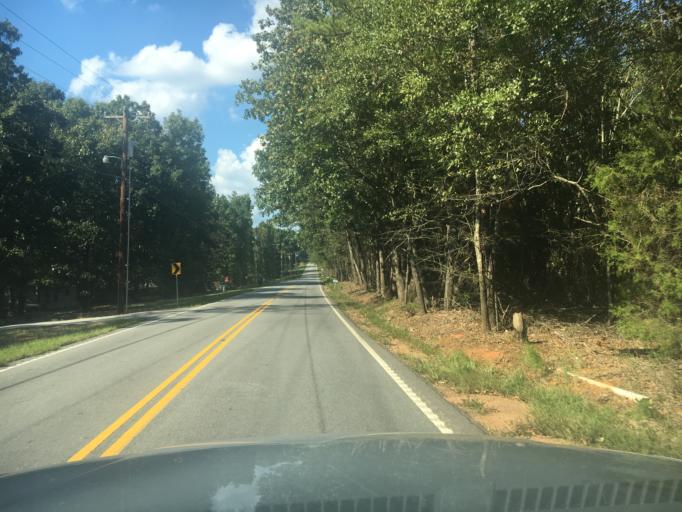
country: US
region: South Carolina
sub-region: Greenville County
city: Fountain Inn
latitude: 34.5623
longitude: -82.2167
